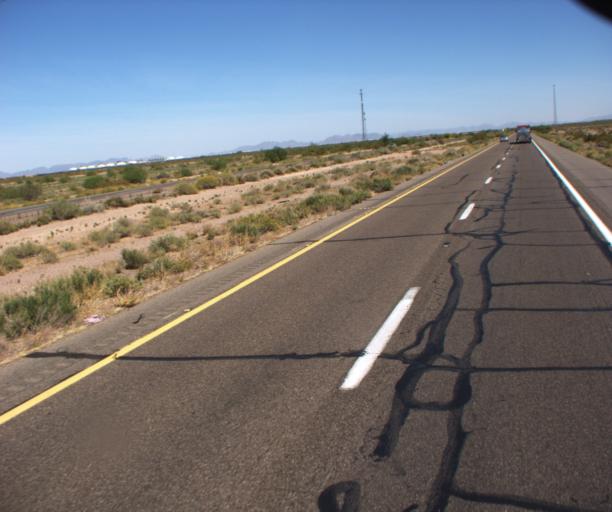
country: US
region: Arizona
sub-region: Maricopa County
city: Gila Bend
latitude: 32.9034
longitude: -112.9965
